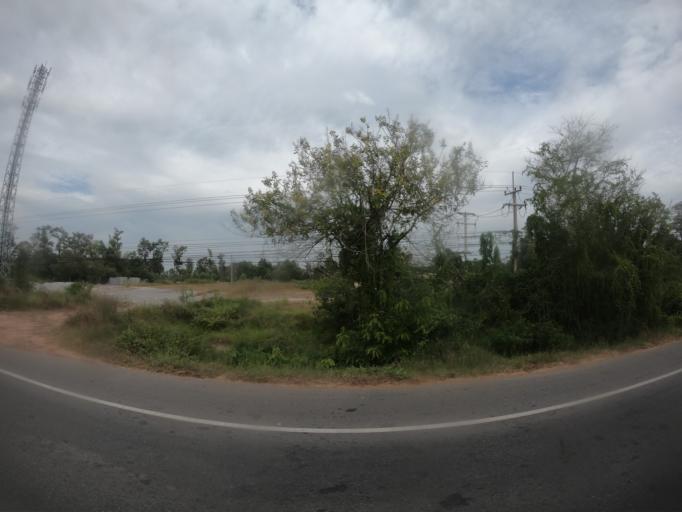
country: TH
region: Roi Et
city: Changhan
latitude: 16.0793
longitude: 103.5791
